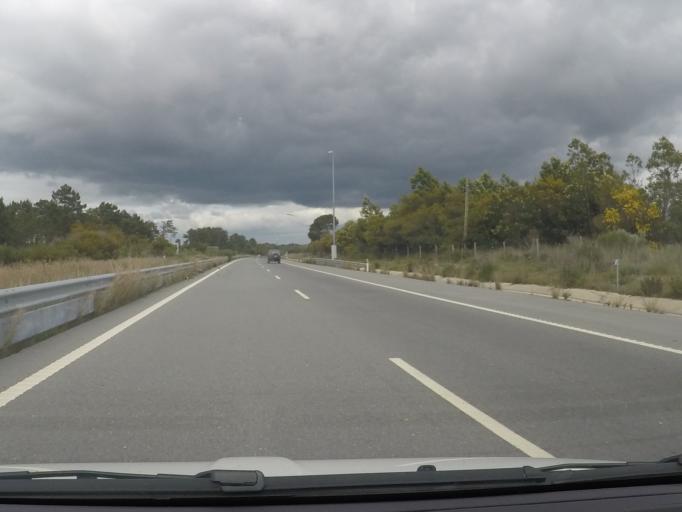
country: PT
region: Setubal
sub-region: Santiago do Cacem
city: Santo Andre
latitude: 37.9845
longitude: -8.7837
